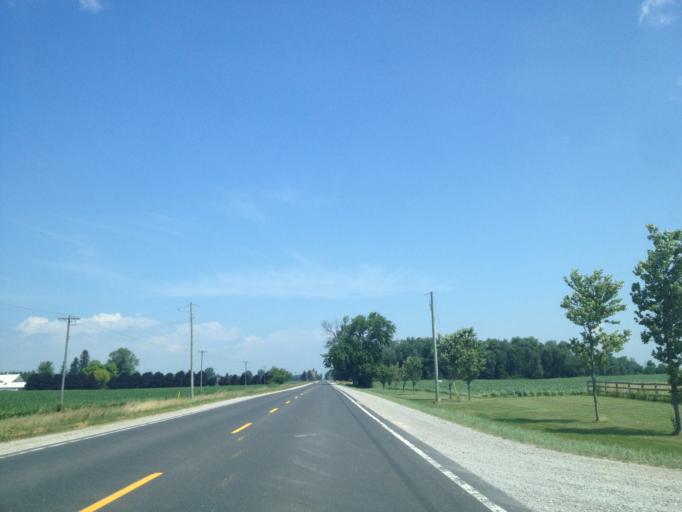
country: CA
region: Ontario
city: Stratford
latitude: 43.3337
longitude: -81.2055
